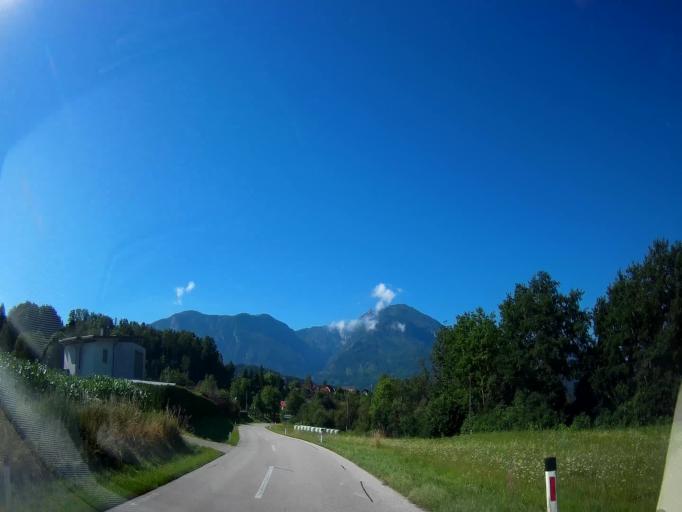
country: AT
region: Carinthia
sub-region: Politischer Bezirk Volkermarkt
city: Gallizien
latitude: 46.5796
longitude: 14.5107
